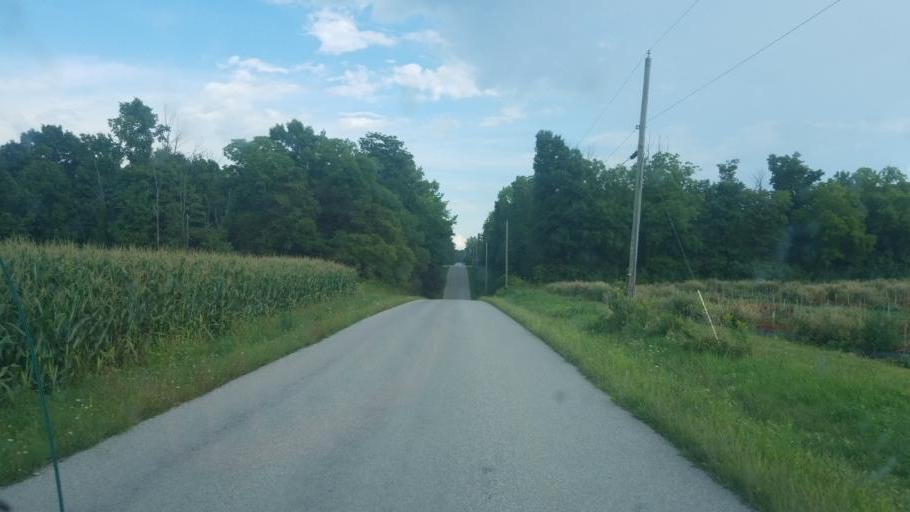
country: US
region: Ohio
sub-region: Huron County
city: Plymouth
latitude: 41.0212
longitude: -82.6630
